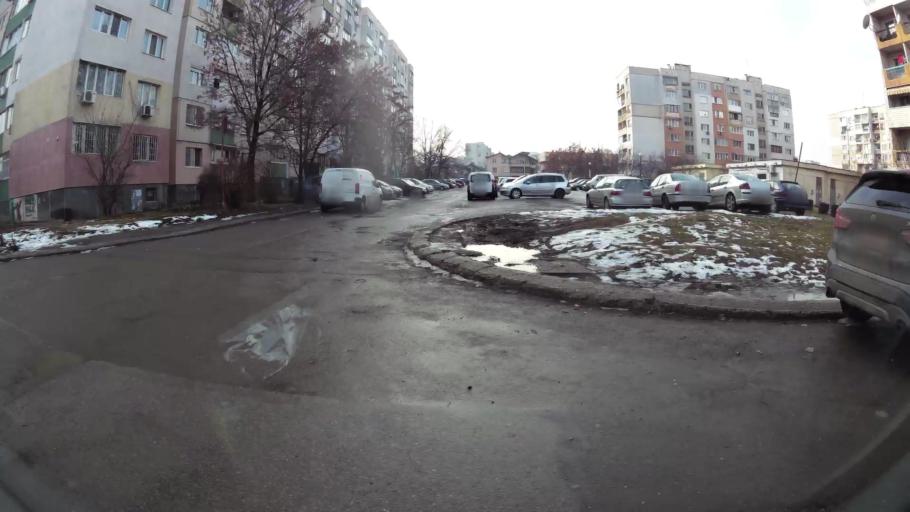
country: BG
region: Sofia-Capital
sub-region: Stolichna Obshtina
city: Sofia
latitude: 42.7195
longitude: 23.2701
